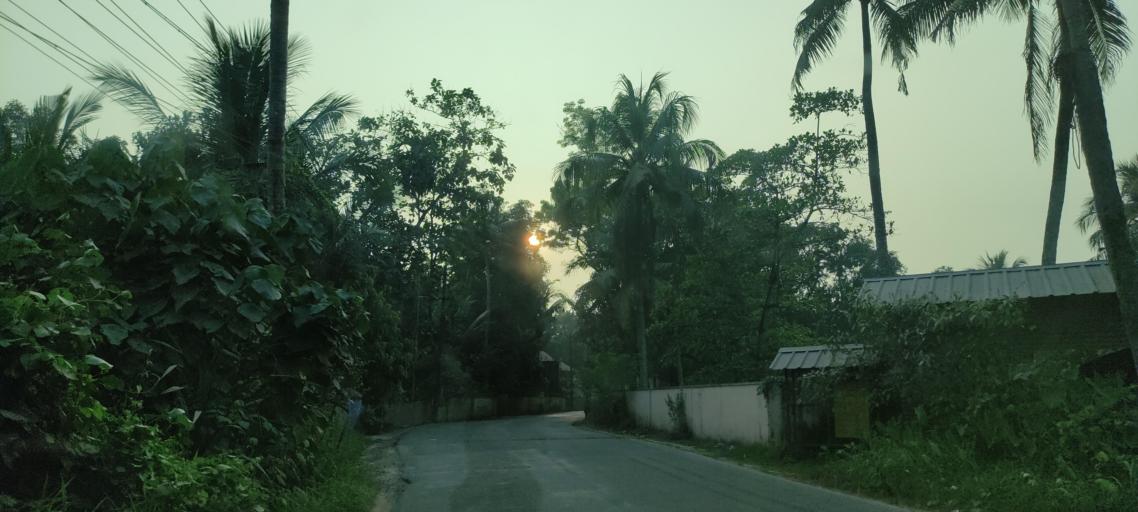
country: IN
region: Kerala
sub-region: Kottayam
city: Vaikam
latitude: 9.6871
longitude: 76.4240
